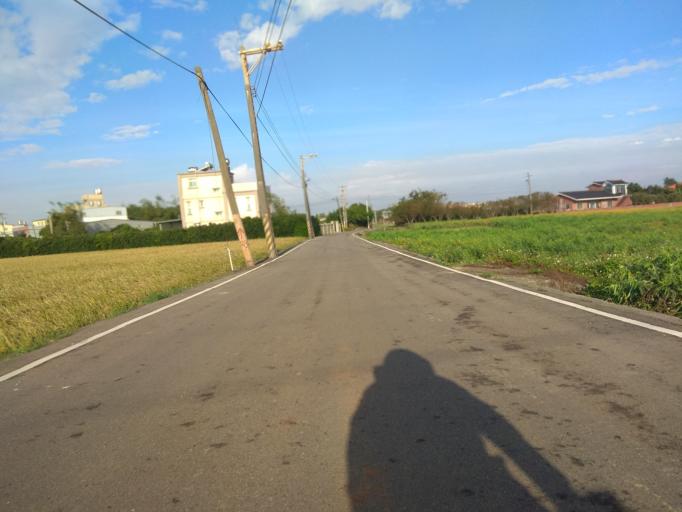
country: TW
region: Taiwan
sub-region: Hsinchu
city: Zhubei
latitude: 24.9783
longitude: 121.0572
